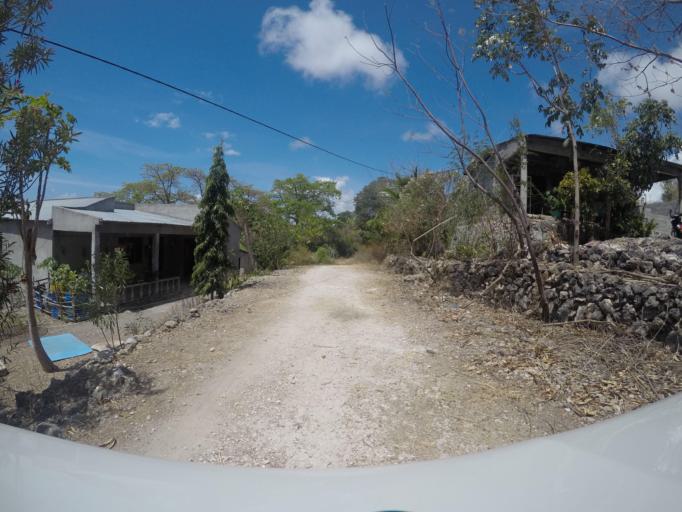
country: TL
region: Baucau
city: Baucau
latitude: -8.4452
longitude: 126.4397
